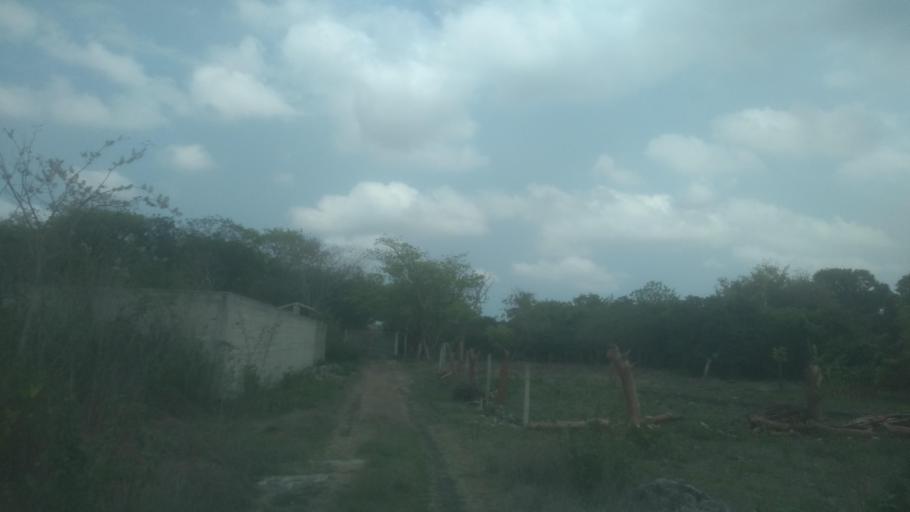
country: MX
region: Veracruz
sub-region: Emiliano Zapata
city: Plan del Rio
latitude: 19.3866
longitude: -96.6328
